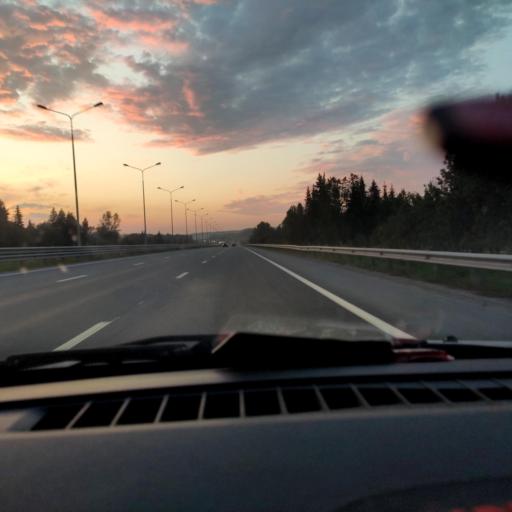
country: RU
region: Perm
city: Kukushtan
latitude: 57.6666
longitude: 56.4377
